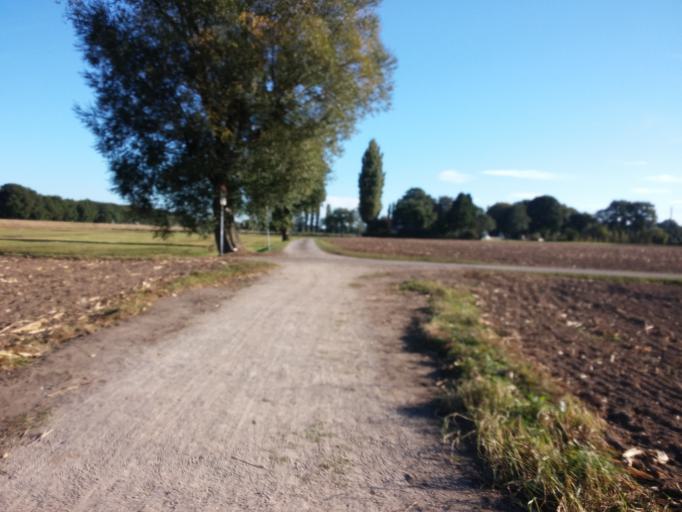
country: DE
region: North Rhine-Westphalia
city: Dorsten
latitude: 51.6521
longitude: 6.9938
